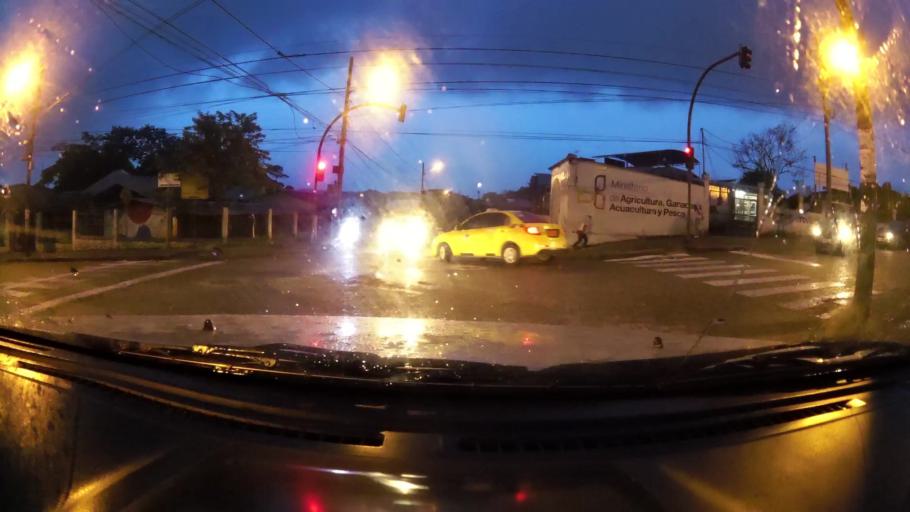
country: EC
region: Pastaza
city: Puyo
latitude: -1.4846
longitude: -78.0023
